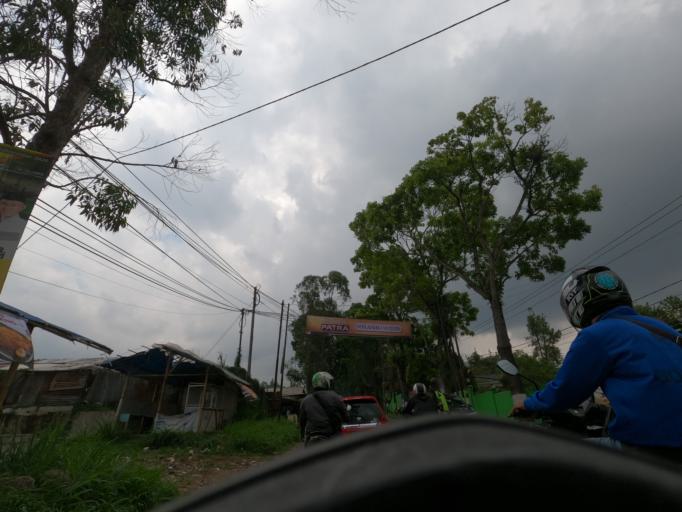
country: ID
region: West Java
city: Sukabumi
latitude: -6.7691
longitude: 107.0589
